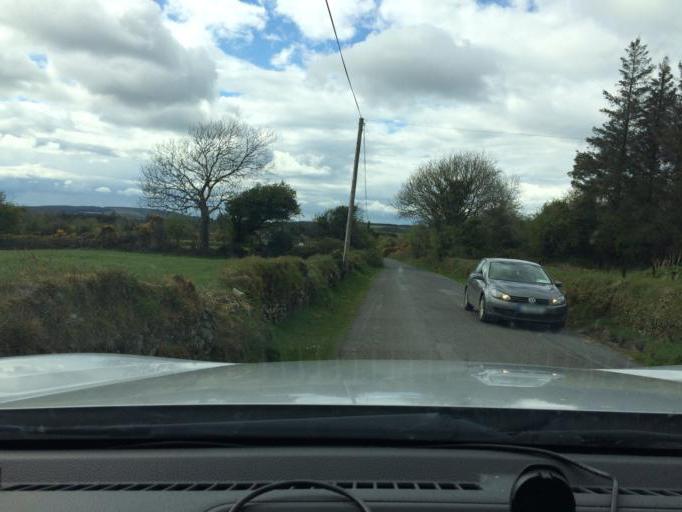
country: IE
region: Munster
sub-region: Waterford
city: Dungarvan
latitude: 52.0433
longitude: -7.6516
